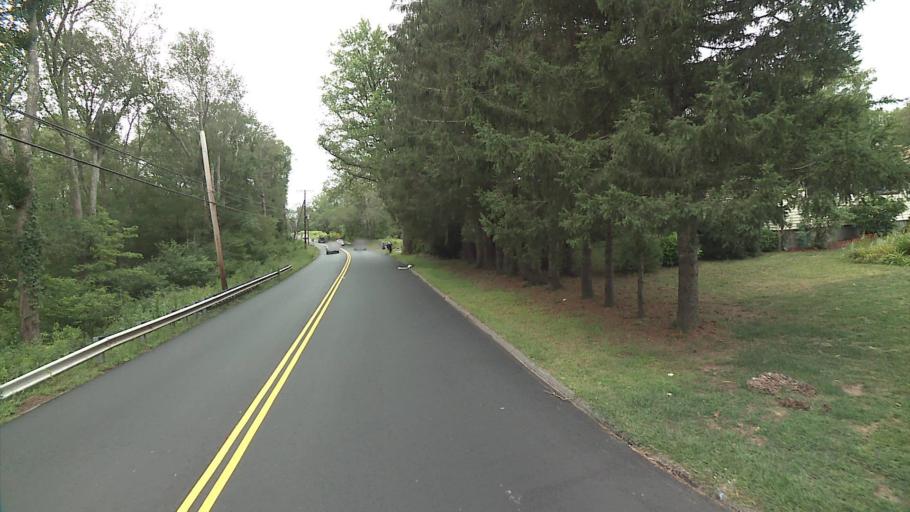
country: US
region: Connecticut
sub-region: New London County
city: Colchester
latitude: 41.5857
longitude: -72.3376
